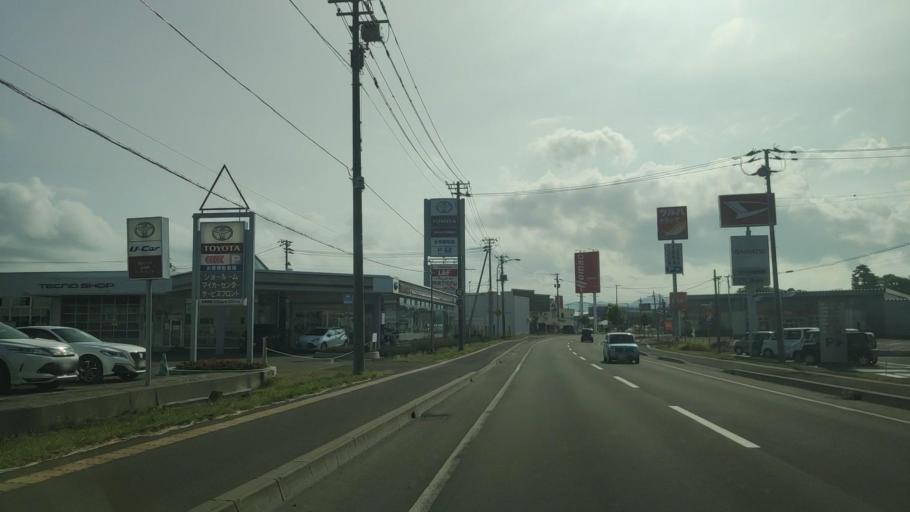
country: JP
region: Hokkaido
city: Shimo-furano
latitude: 43.3452
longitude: 142.3783
